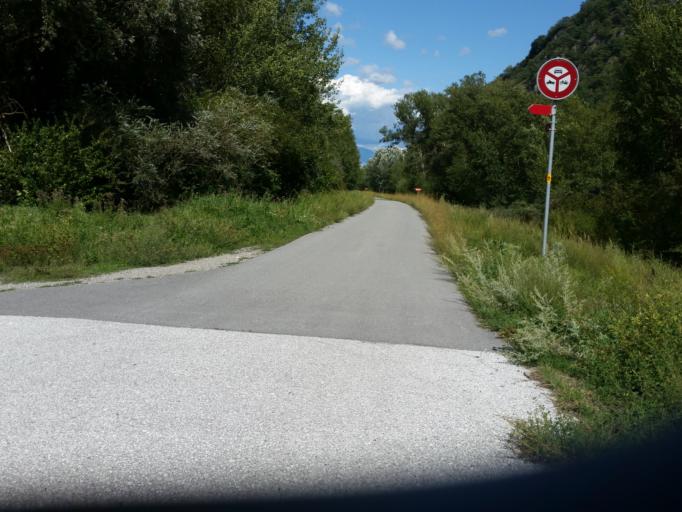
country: CH
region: Valais
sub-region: Conthey District
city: Ardon
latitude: 46.1850
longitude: 7.2523
